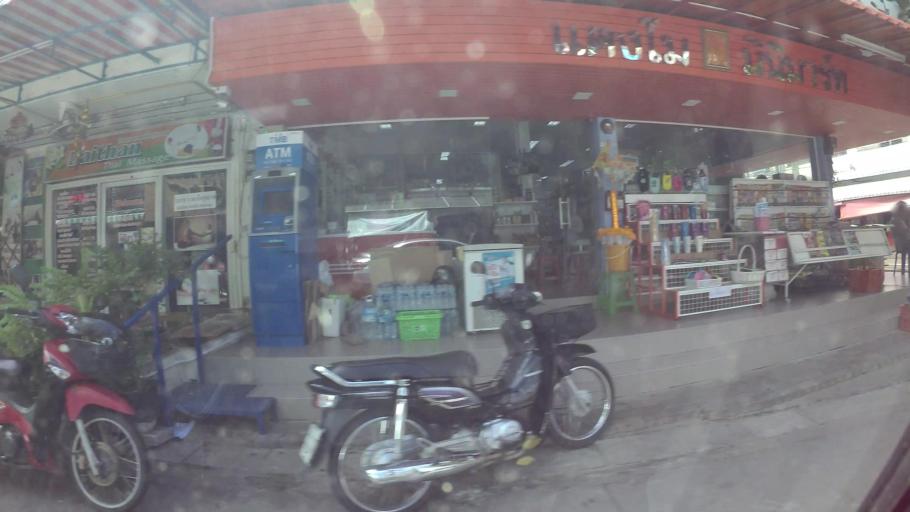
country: TH
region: Chon Buri
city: Phatthaya
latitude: 12.9331
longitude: 100.8876
